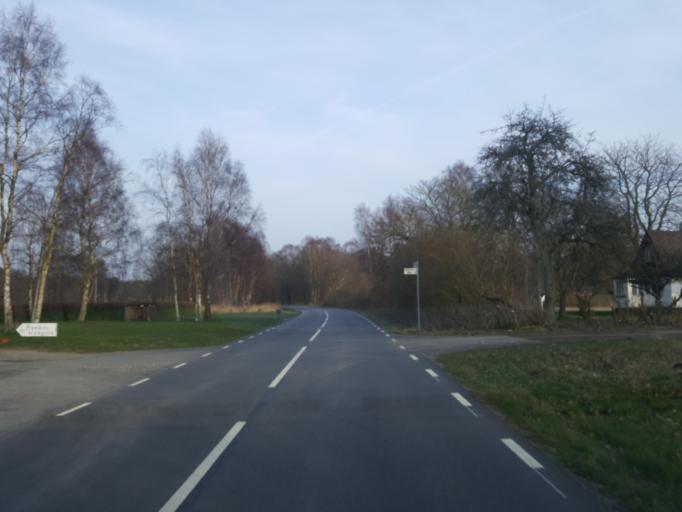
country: SE
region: Skane
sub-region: Ystads Kommun
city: Kopingebro
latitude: 55.3936
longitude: 14.1657
